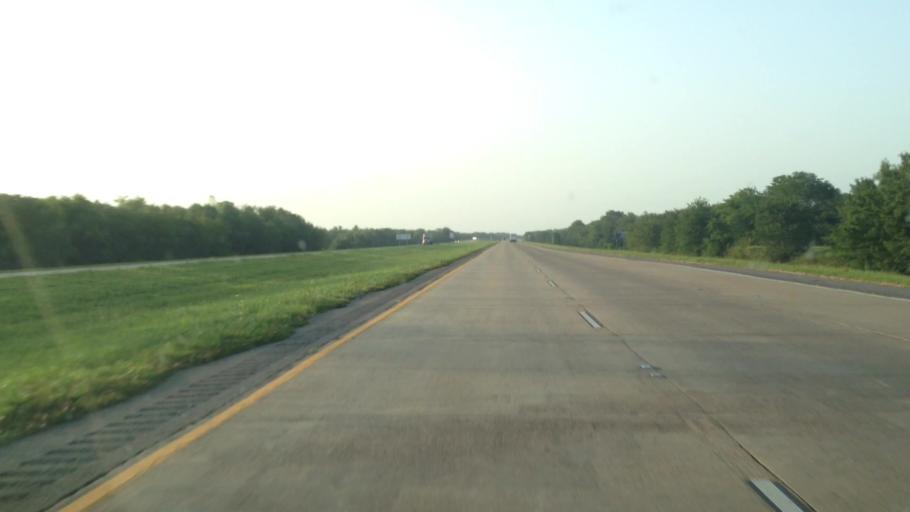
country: US
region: Louisiana
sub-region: Natchitoches Parish
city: Vienna Bend
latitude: 31.6032
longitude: -93.0442
